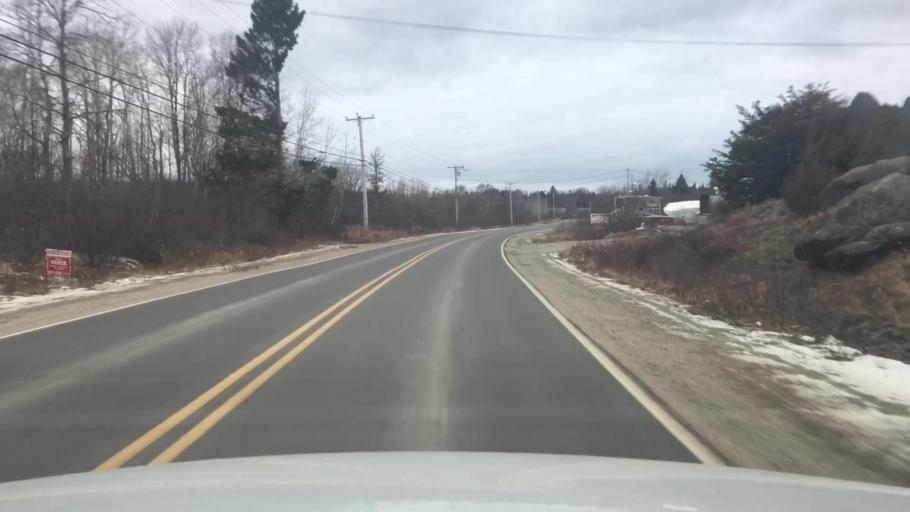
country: US
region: Maine
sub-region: Washington County
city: Jonesport
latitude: 44.5537
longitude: -67.6250
